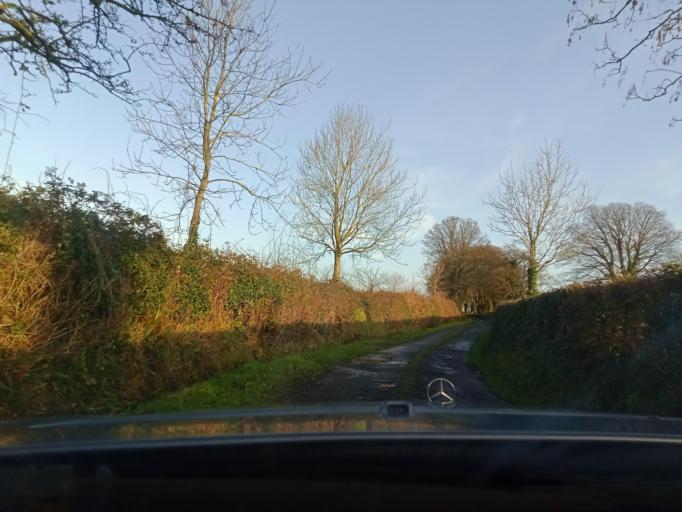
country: IE
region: Leinster
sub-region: Kilkenny
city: Callan
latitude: 52.4775
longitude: -7.4437
